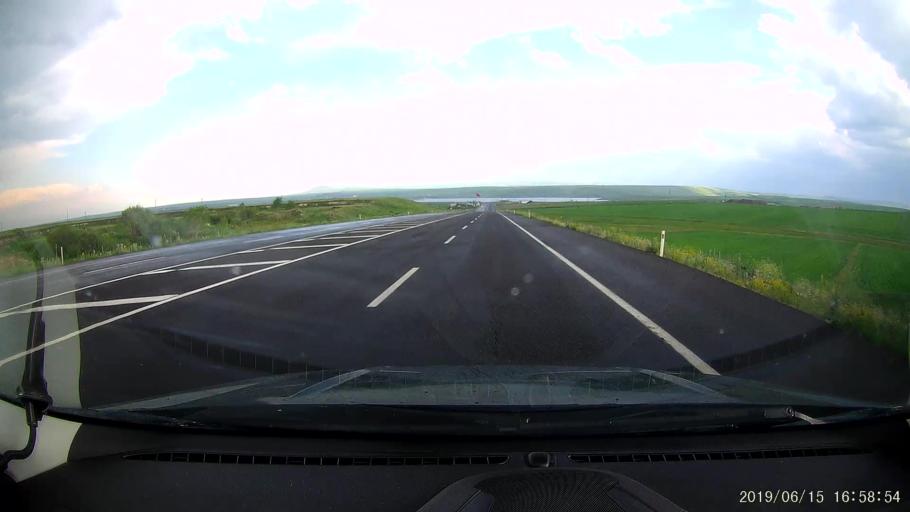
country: TR
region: Kars
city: Susuz
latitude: 40.7587
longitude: 43.1467
